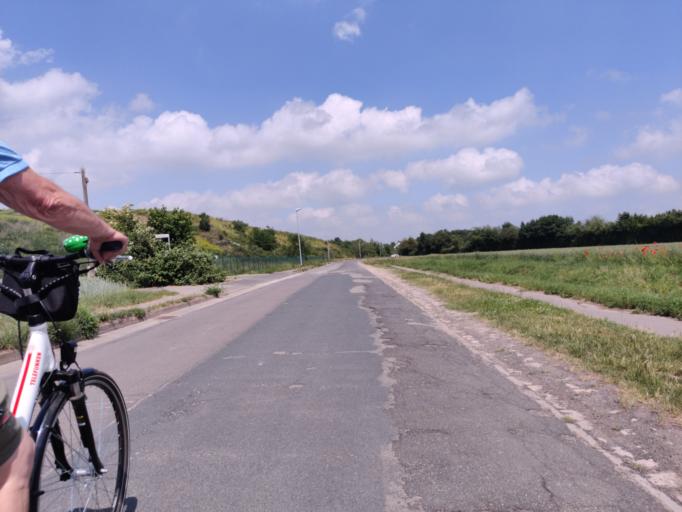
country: DE
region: Lower Saxony
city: Hildesheim
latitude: 52.1705
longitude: 9.9592
